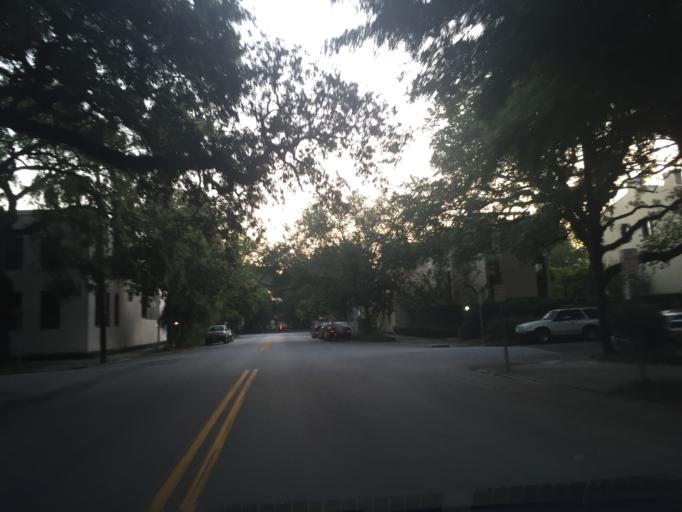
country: US
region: Georgia
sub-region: Chatham County
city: Savannah
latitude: 32.0710
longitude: -81.0901
